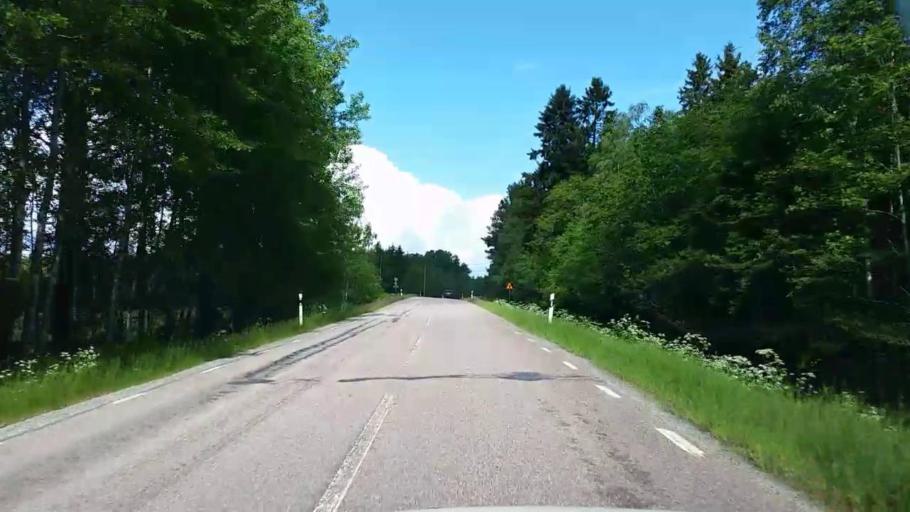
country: SE
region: Vaestmanland
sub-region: Fagersta Kommun
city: Fagersta
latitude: 59.9454
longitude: 15.7999
